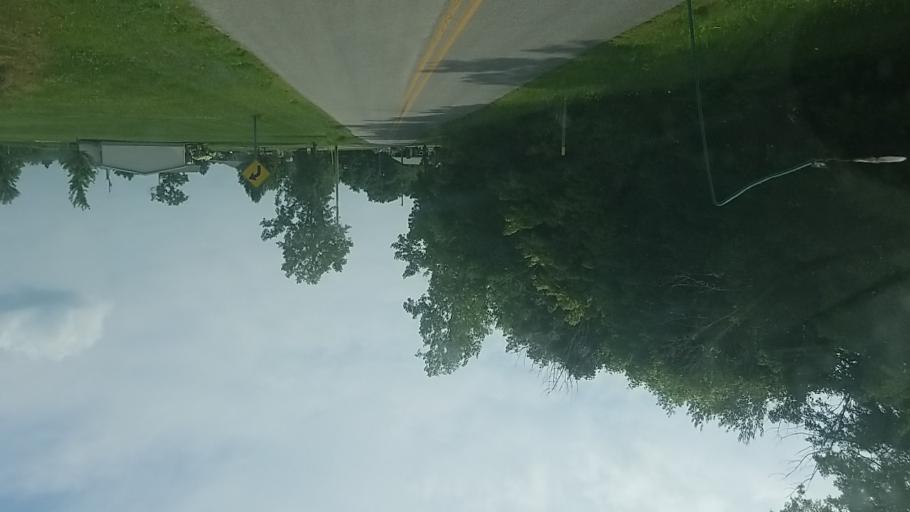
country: US
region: Ohio
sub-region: Hardin County
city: Forest
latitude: 40.8008
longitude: -83.5515
